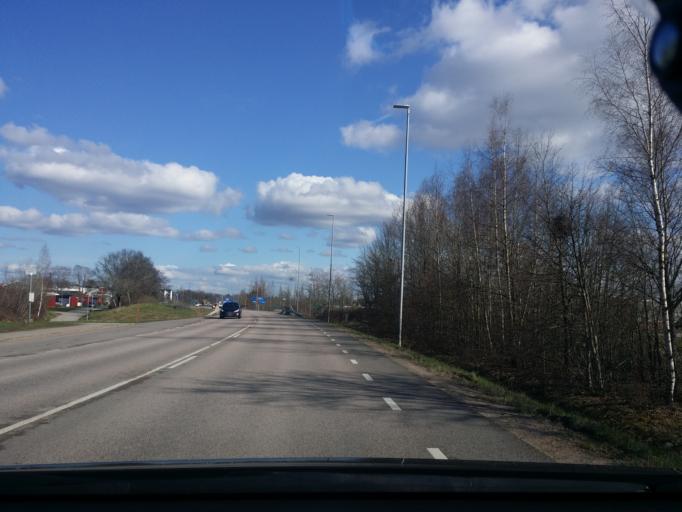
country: SE
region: Vaestmanland
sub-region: Sala Kommun
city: Sala
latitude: 59.9232
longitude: 16.5808
